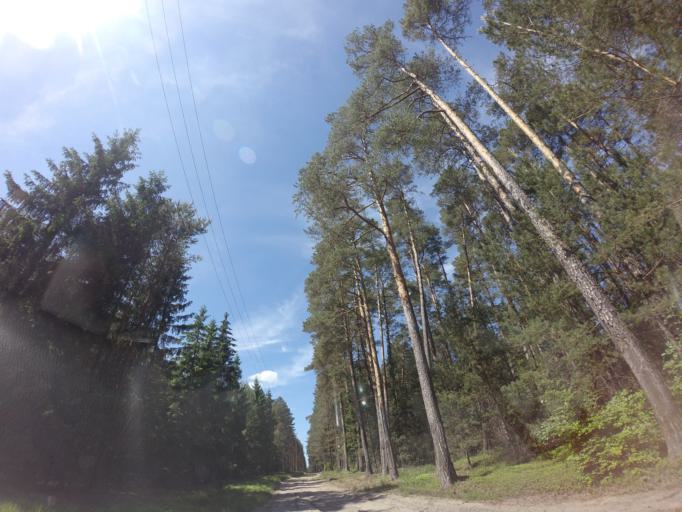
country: PL
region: West Pomeranian Voivodeship
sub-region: Powiat choszczenski
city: Drawno
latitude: 53.1216
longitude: 15.8035
